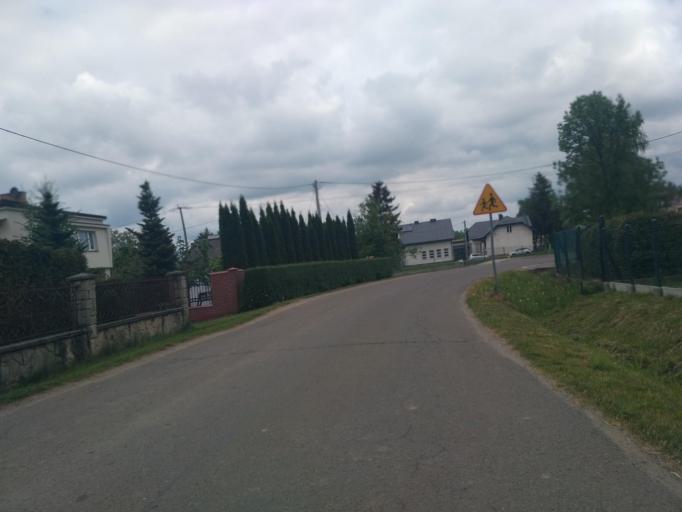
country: PL
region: Subcarpathian Voivodeship
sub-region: Powiat jasielski
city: Tarnowiec
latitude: 49.7102
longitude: 21.5795
